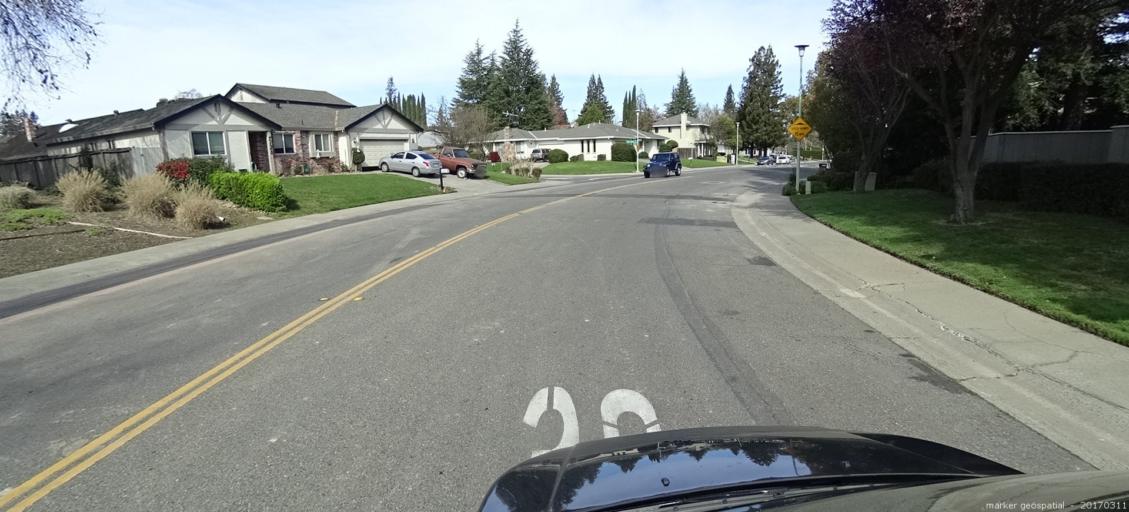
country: US
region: California
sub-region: Yolo County
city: West Sacramento
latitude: 38.4966
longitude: -121.5532
